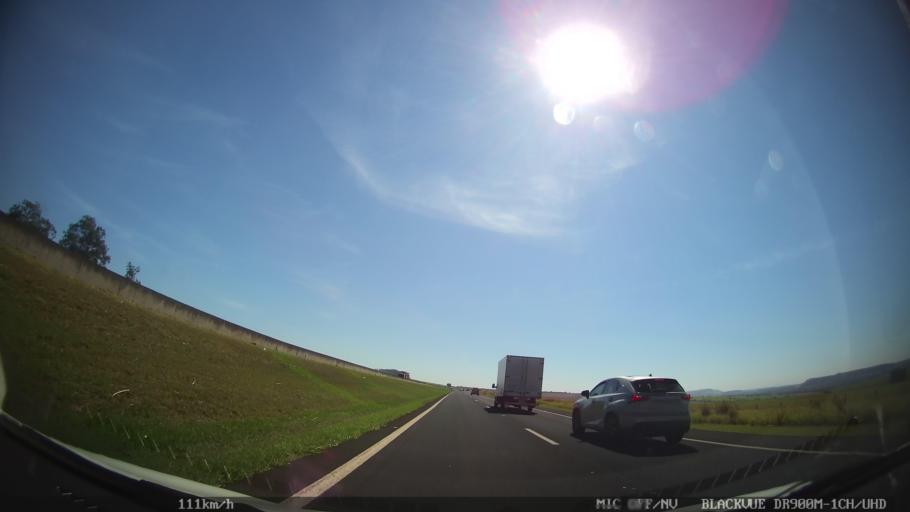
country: BR
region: Sao Paulo
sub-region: Sao Simao
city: Sao Simao
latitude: -21.4512
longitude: -47.6466
